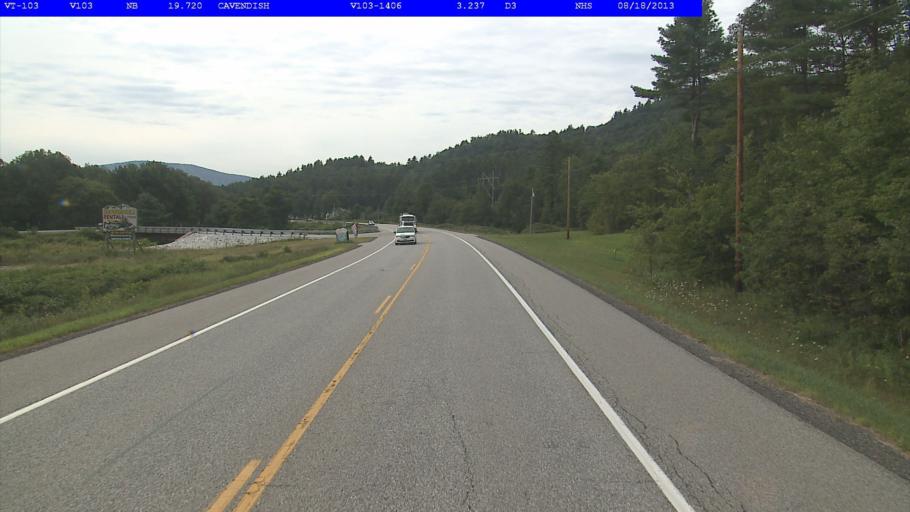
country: US
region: Vermont
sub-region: Windsor County
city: Chester
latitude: 43.3871
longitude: -72.6523
